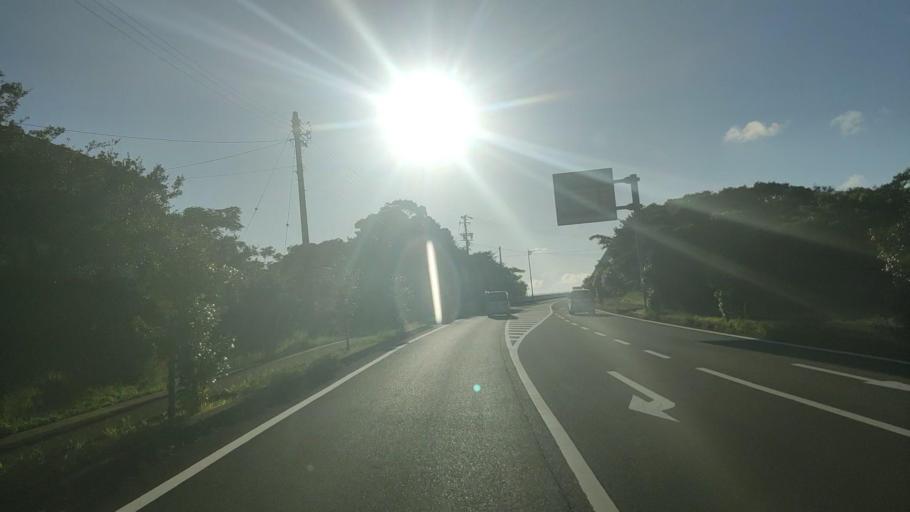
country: JP
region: Mie
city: Toba
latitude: 34.2640
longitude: 136.8171
